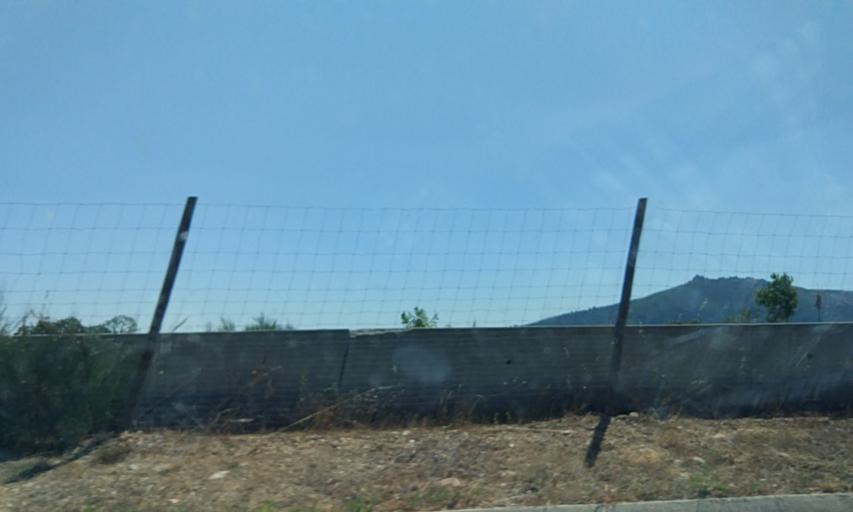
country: PT
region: Braganca
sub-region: Braganca Municipality
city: Braganca
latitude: 41.6927
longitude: -6.8117
